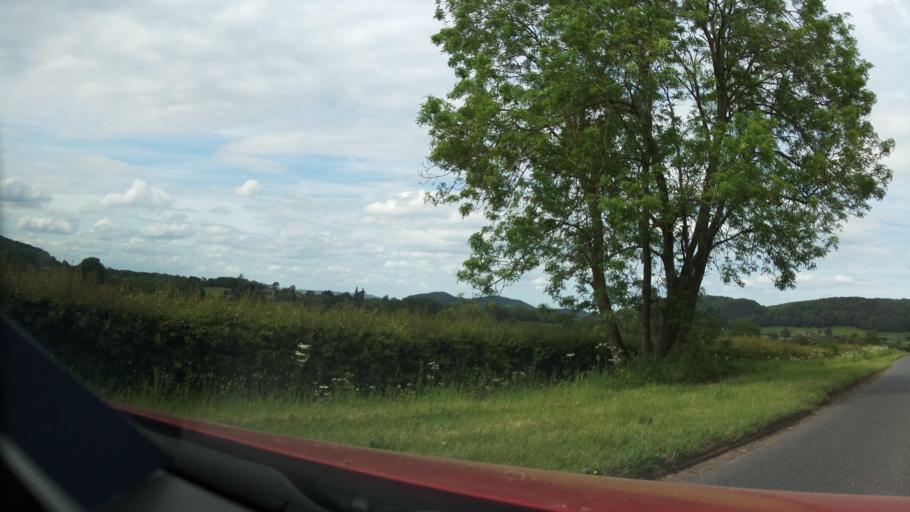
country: GB
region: England
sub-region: Herefordshire
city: Evesbatch
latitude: 52.1262
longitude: -2.4008
